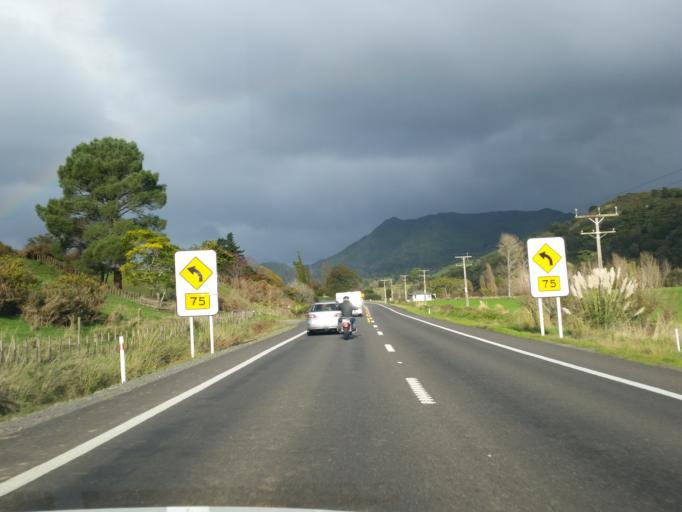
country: NZ
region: Waikato
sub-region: Hauraki District
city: Paeroa
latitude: -37.4007
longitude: 175.6970
